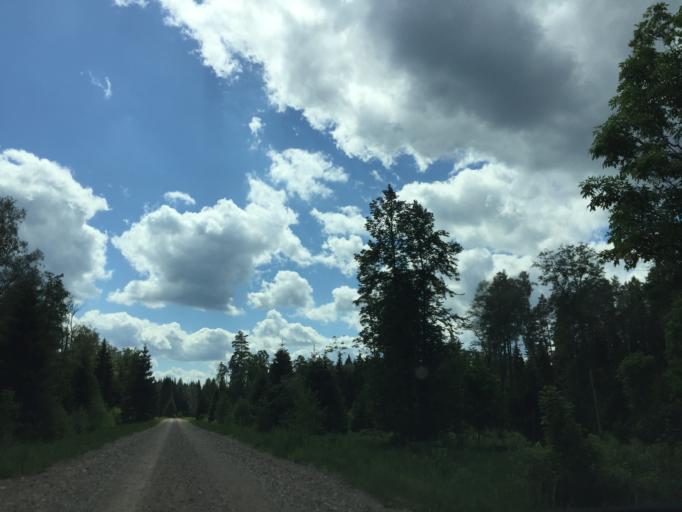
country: LV
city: Tireli
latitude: 56.8392
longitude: 23.6980
